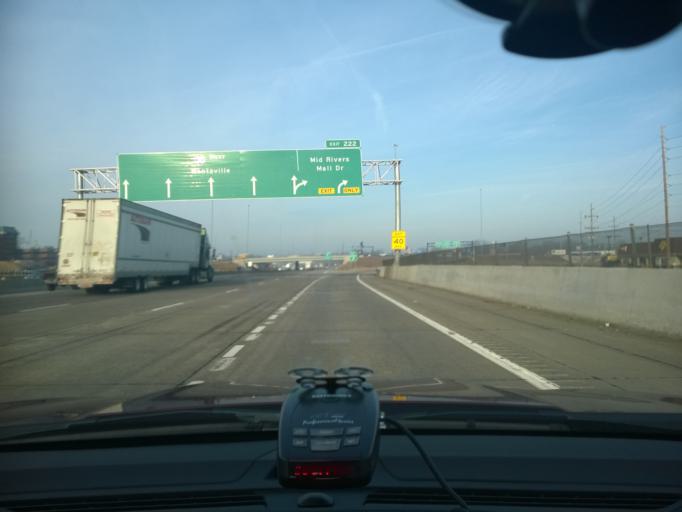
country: US
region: Missouri
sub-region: Saint Charles County
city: Saint Peters
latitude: 38.7997
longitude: -90.6169
